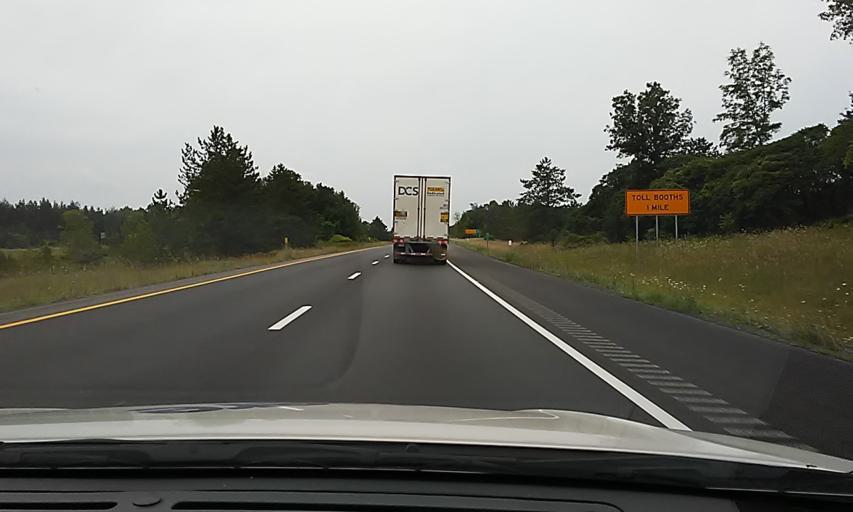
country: US
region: New York
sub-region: Genesee County
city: Bergen
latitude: 43.0438
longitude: -77.9533
